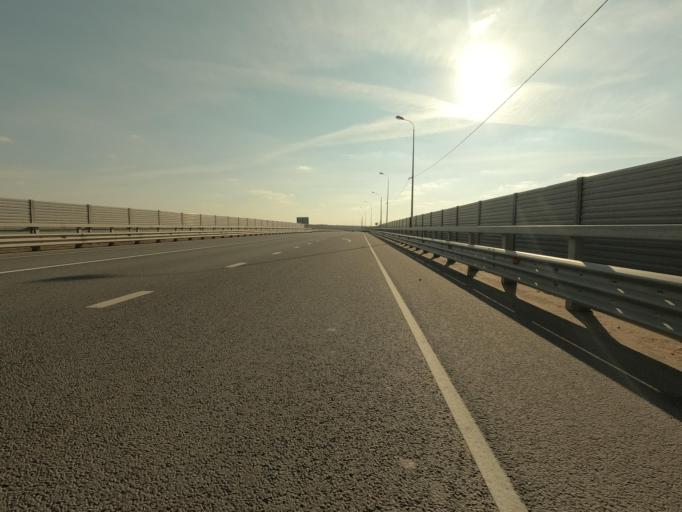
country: RU
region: Leningrad
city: Mga
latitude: 59.7550
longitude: 31.0920
